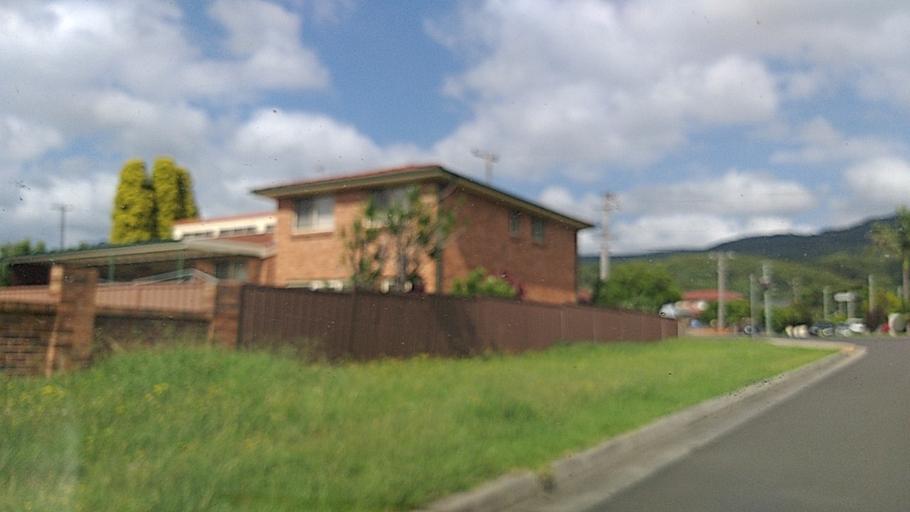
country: AU
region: New South Wales
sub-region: Wollongong
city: Corrimal
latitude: -34.3755
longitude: 150.8899
